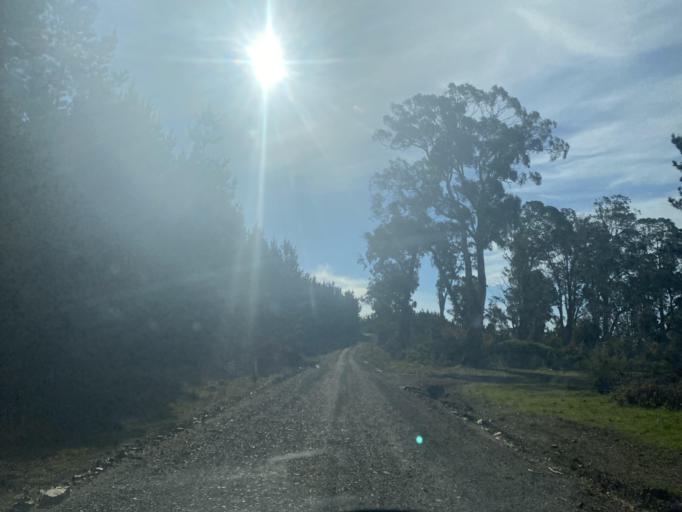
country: AU
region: Victoria
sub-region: Mansfield
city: Mansfield
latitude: -36.8720
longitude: 146.1806
